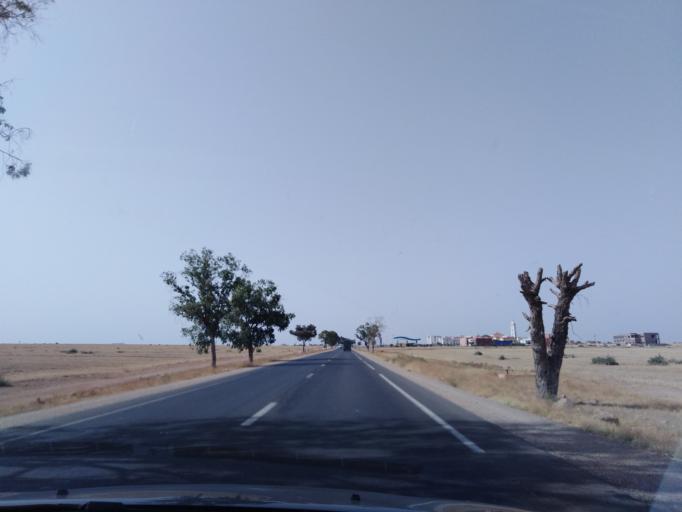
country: MA
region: Marrakech-Tensift-Al Haouz
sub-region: Kelaa-Des-Sraghna
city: Sidi Bou Othmane
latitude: 32.2139
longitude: -7.9568
